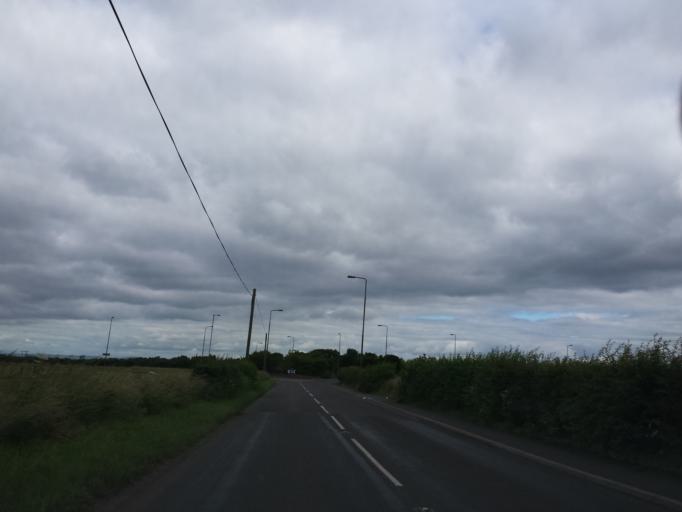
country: GB
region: Scotland
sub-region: East Lothian
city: Musselburgh
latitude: 55.9224
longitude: -3.0323
